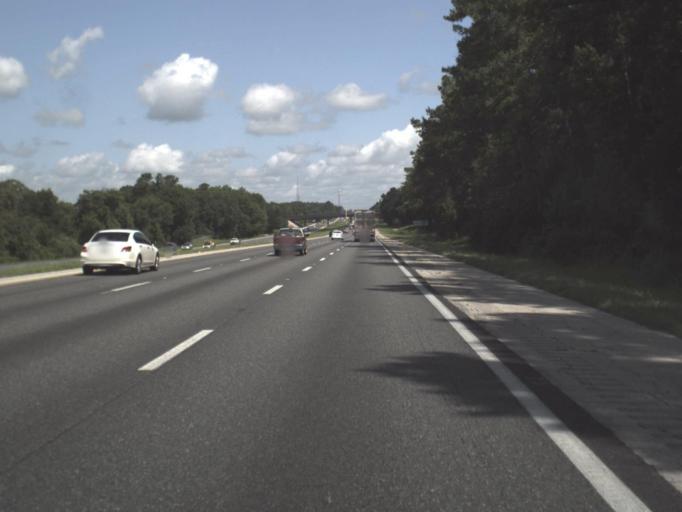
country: US
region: Florida
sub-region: Alachua County
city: Alachua
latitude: 29.6695
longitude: -82.4274
